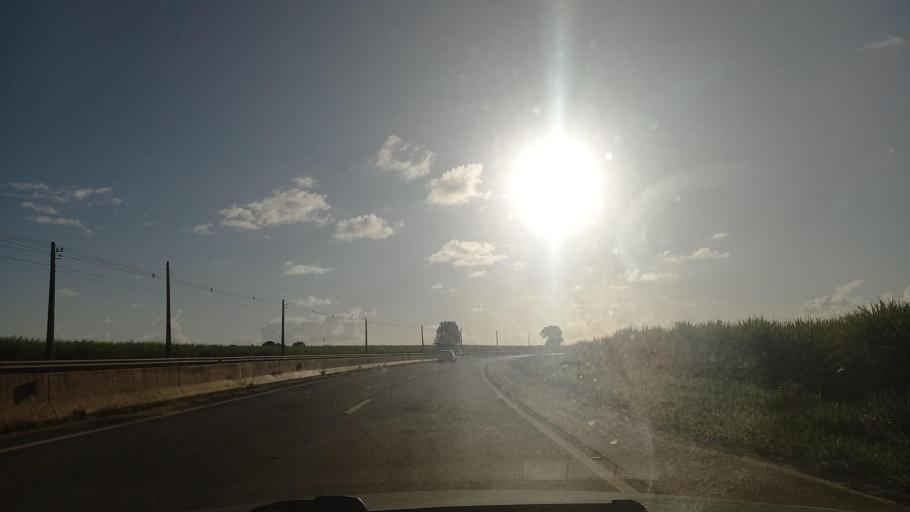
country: BR
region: Alagoas
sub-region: Campo Alegre
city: Campo Alegre
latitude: -9.8232
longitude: -36.2409
